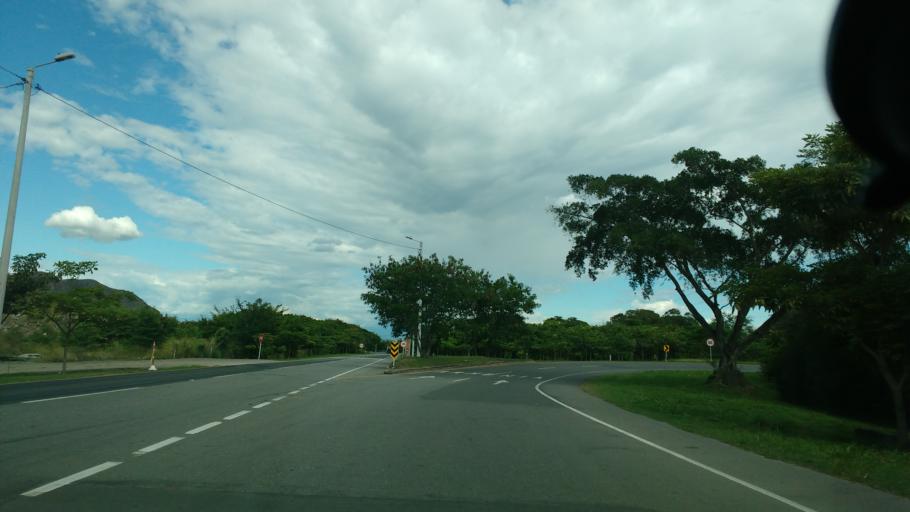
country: CO
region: Tolima
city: Valle de San Juan
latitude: 4.3245
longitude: -75.0753
